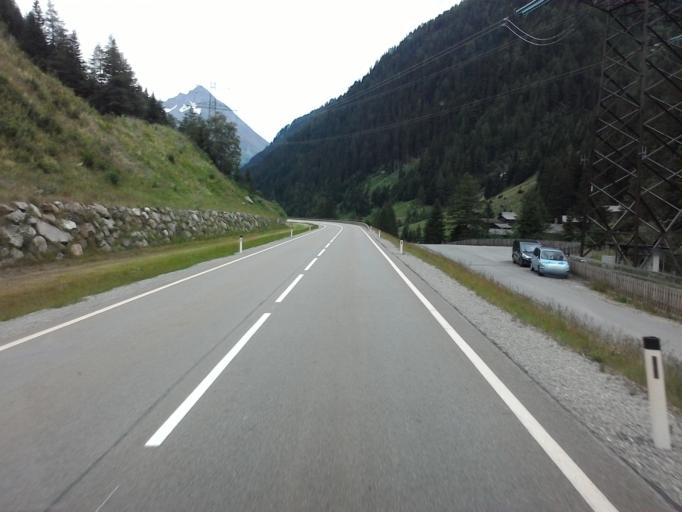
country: AT
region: Tyrol
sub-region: Politischer Bezirk Lienz
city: Matrei in Osttirol
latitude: 47.1062
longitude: 12.5058
